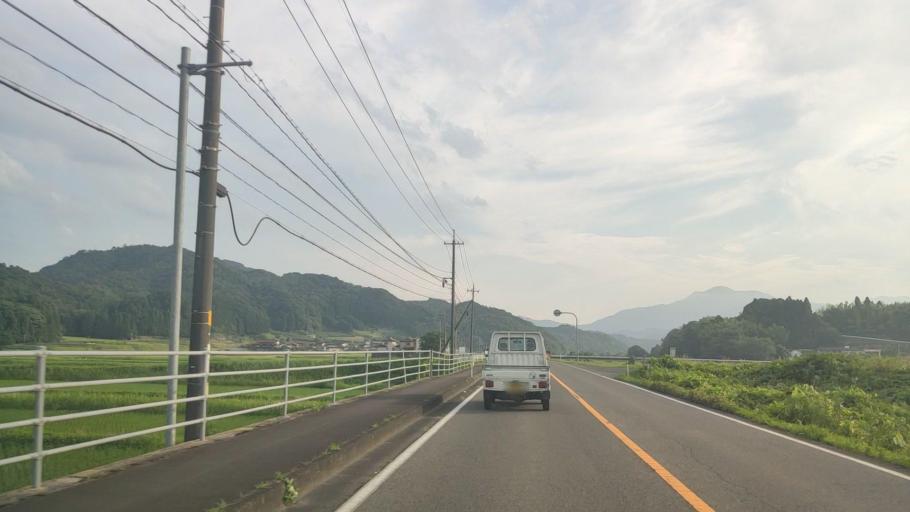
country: JP
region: Tottori
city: Kurayoshi
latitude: 35.3802
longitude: 133.7760
